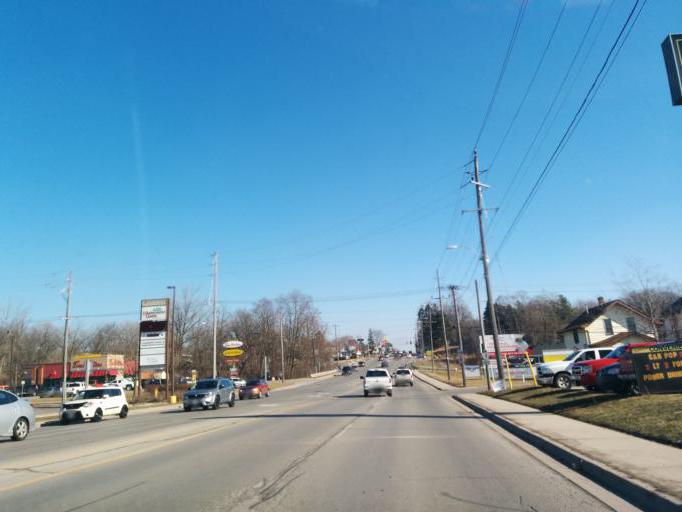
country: CA
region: Ontario
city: Norfolk County
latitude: 42.8462
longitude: -80.3065
